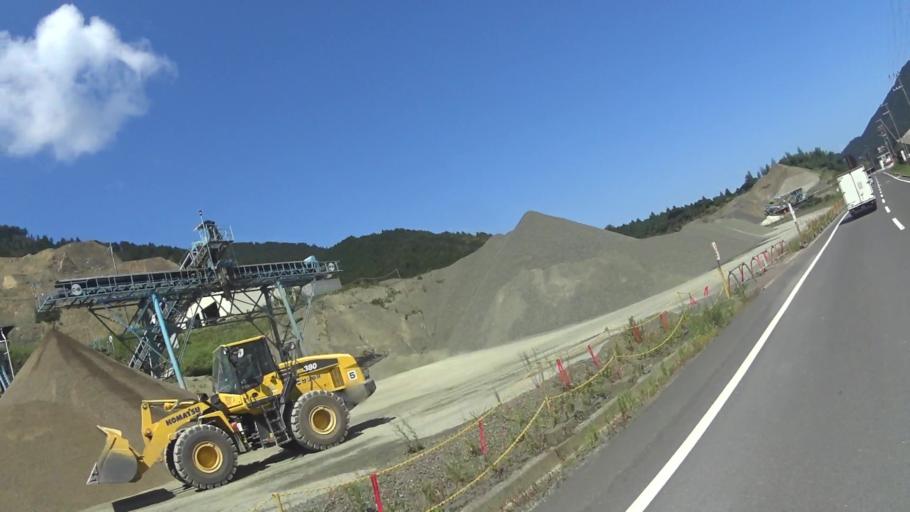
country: JP
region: Kyoto
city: Maizuru
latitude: 35.4888
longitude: 135.2808
